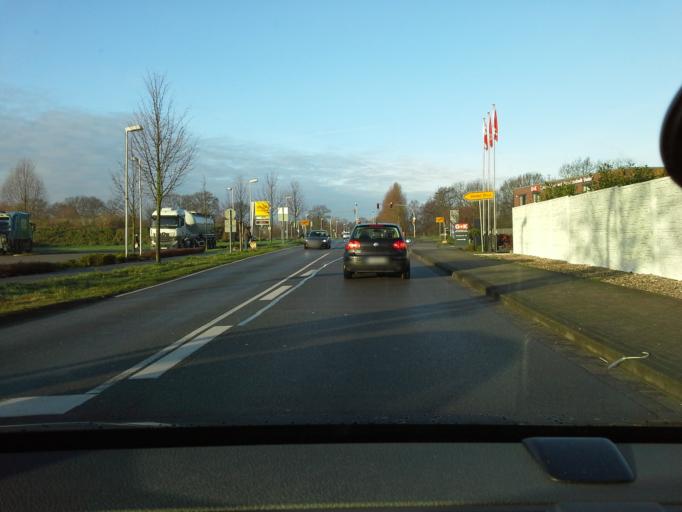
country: DE
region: Schleswig-Holstein
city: Pinneberg
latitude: 53.6577
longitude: 9.7760
